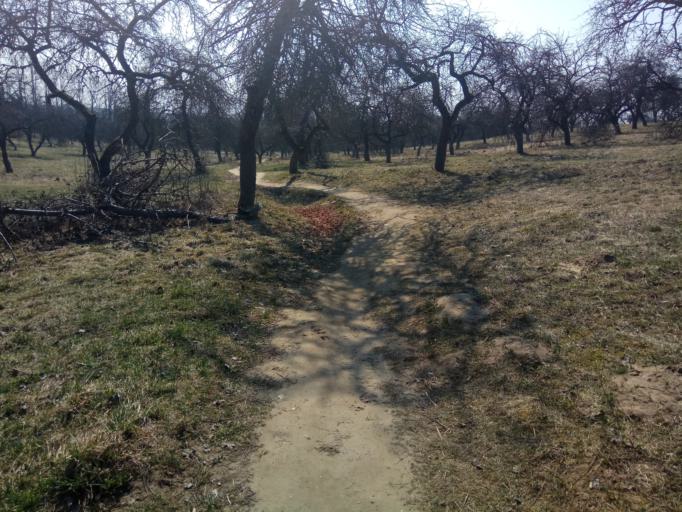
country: BY
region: Minsk
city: Valozhyn
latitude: 54.0845
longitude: 26.5171
